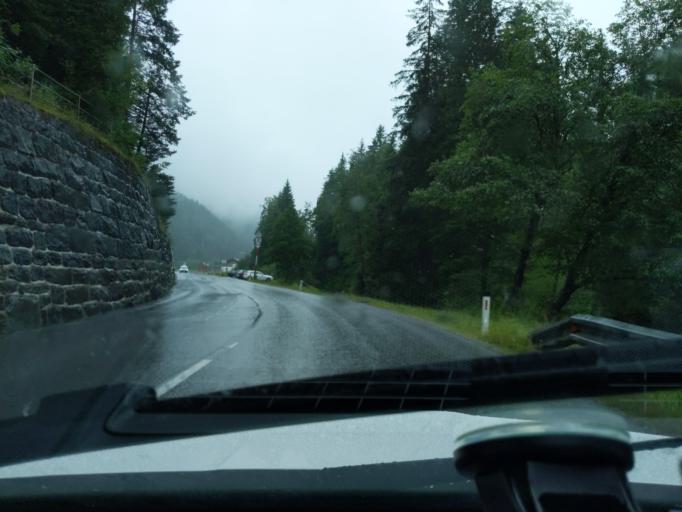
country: AT
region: Tyrol
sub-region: Politischer Bezirk Schwaz
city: Mayrhofen
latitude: 47.1449
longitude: 11.7196
